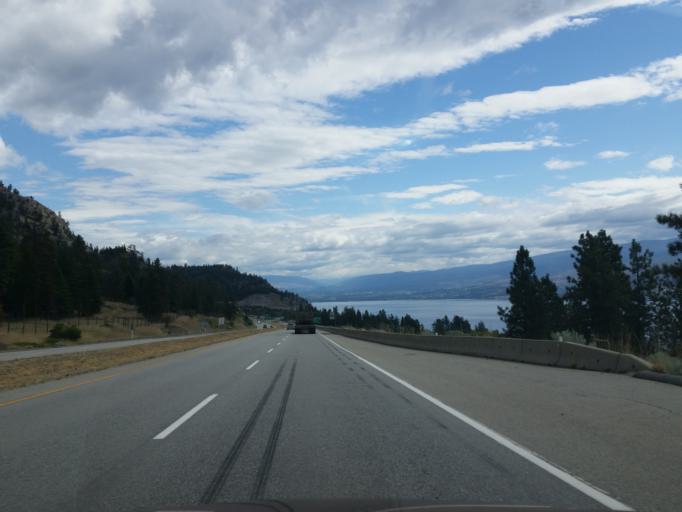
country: CA
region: British Columbia
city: Peachland
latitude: 49.8012
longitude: -119.6855
